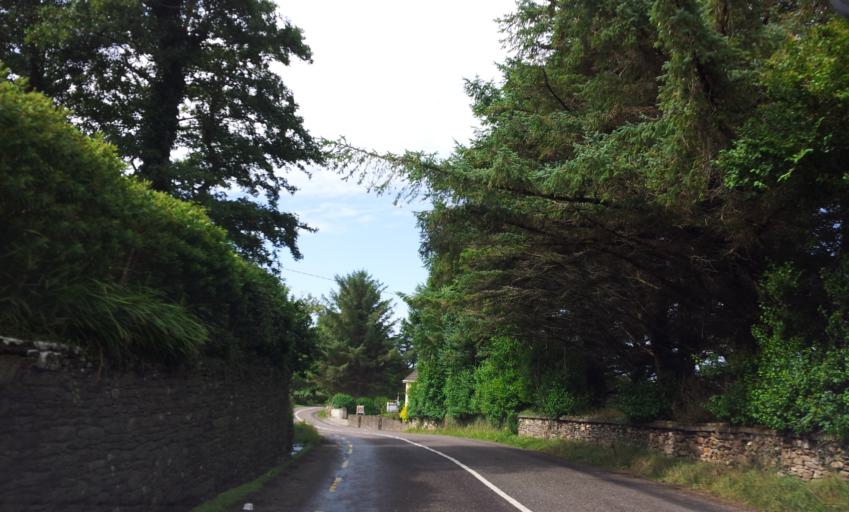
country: IE
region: Munster
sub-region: Ciarrai
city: Killorglin
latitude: 52.0553
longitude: -9.9649
